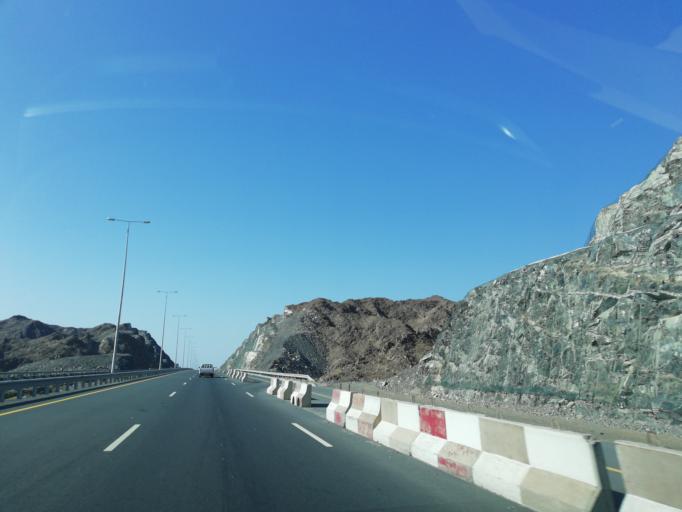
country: OM
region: Muhafazat ad Dakhiliyah
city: Sufalat Sama'il
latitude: 22.9990
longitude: 58.2309
